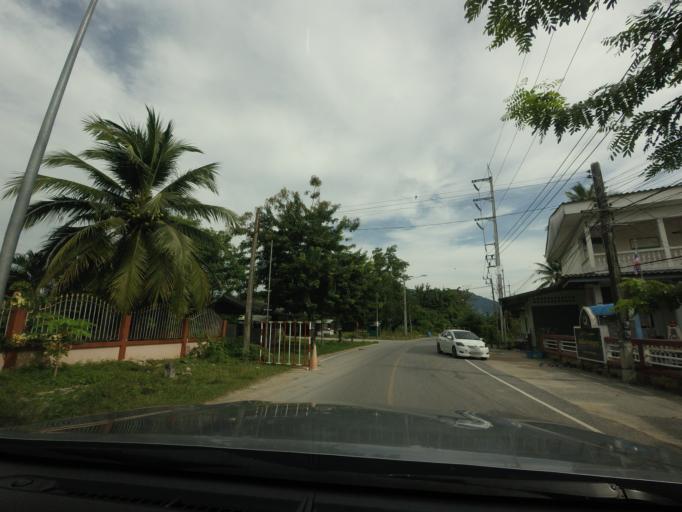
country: TH
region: Yala
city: Yala
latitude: 6.5157
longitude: 101.2895
